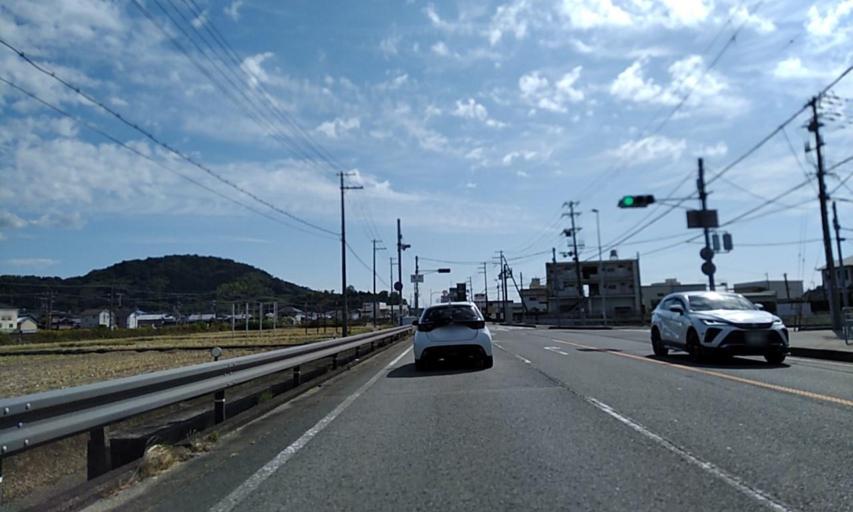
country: JP
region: Wakayama
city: Gobo
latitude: 33.9198
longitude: 135.1464
